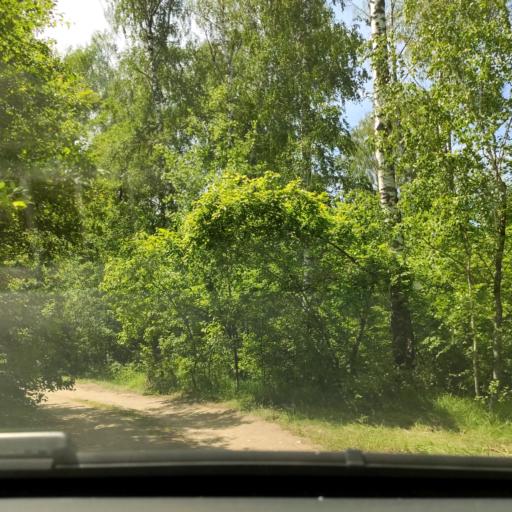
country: RU
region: Voronezj
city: Podgornoye
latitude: 51.8048
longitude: 39.1483
